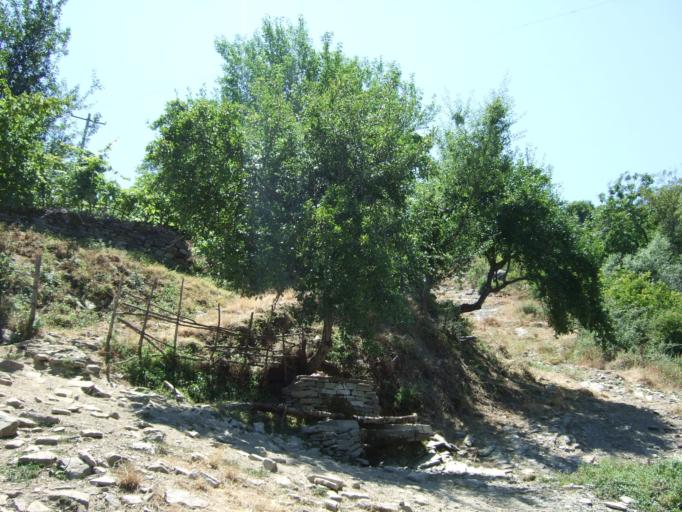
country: AL
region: Gjirokaster
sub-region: Rrethi i Permetit
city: Frasher
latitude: 40.3142
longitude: 20.4584
